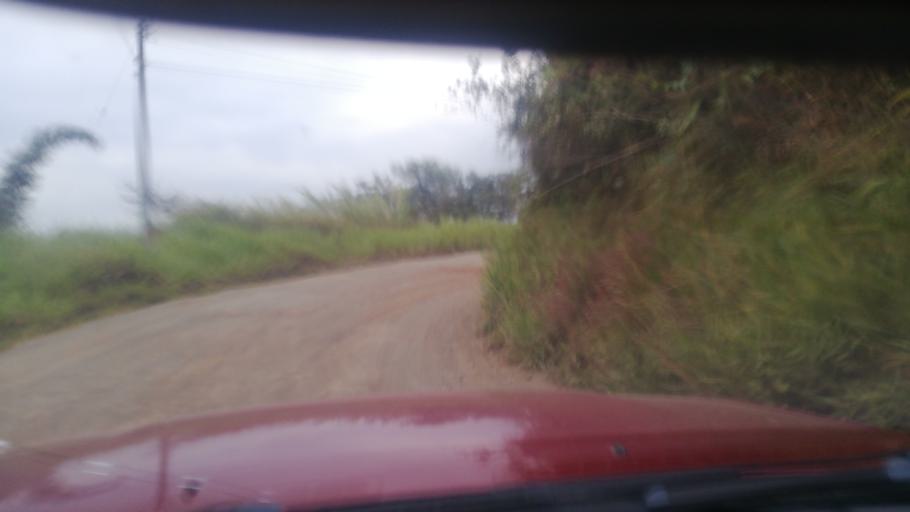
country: CO
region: Valle del Cauca
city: Cali
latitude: 3.4918
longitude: -76.5452
